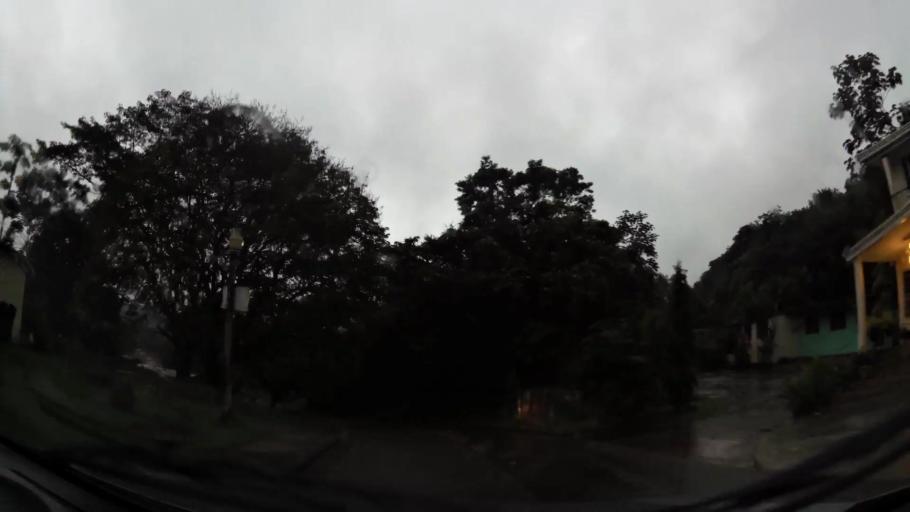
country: PA
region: Panama
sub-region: Distrito de Panama
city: Paraiso
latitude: 9.0345
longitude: -79.6285
